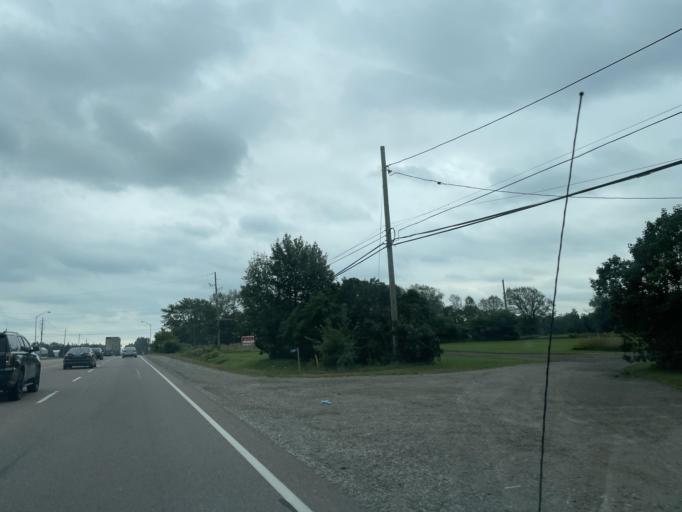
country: CA
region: Ontario
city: Burlington
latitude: 43.3322
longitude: -79.9454
